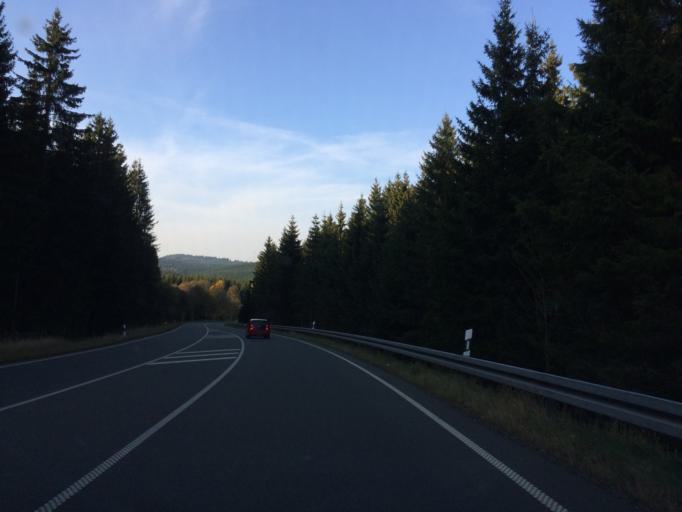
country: DE
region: Lower Saxony
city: Braunlage
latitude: 51.7082
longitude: 10.5936
